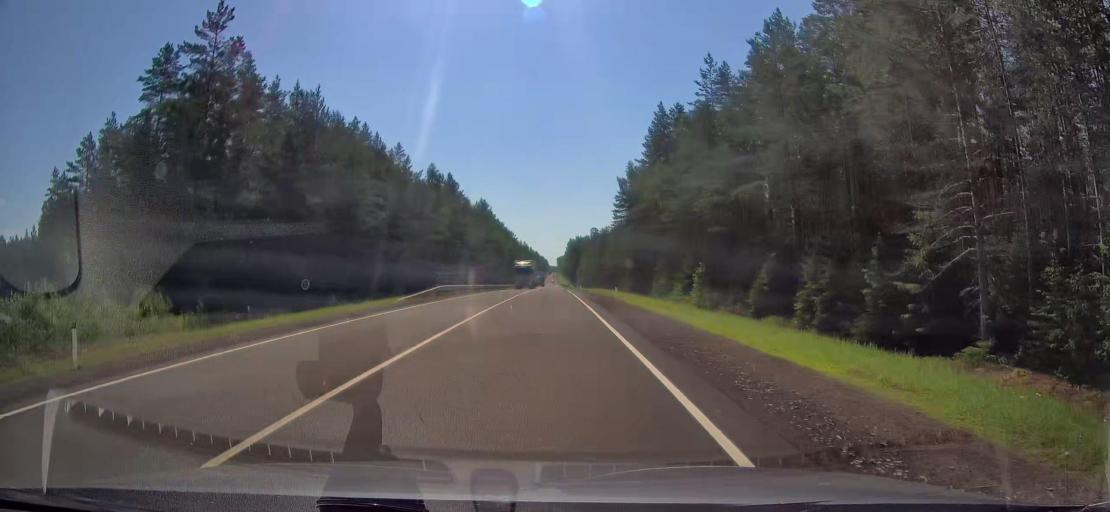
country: RU
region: Leningrad
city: Yefimovskiy
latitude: 59.3754
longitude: 34.7969
